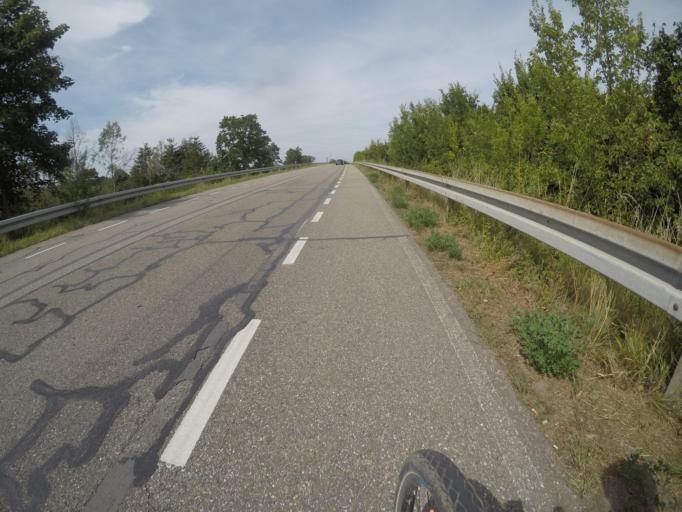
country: DE
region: Baden-Wuerttemberg
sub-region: Karlsruhe Region
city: Waghausel
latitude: 49.2395
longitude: 8.5072
